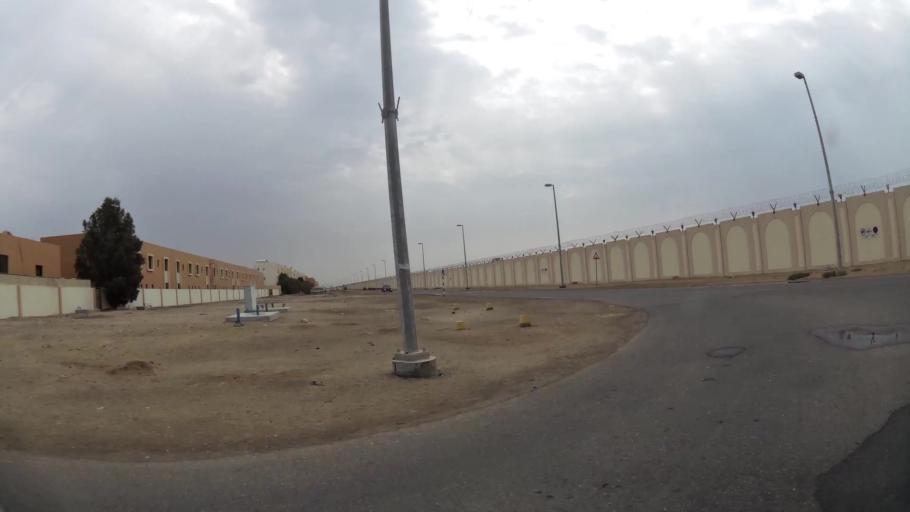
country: AE
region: Abu Dhabi
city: Abu Dhabi
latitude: 24.4373
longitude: 54.4487
